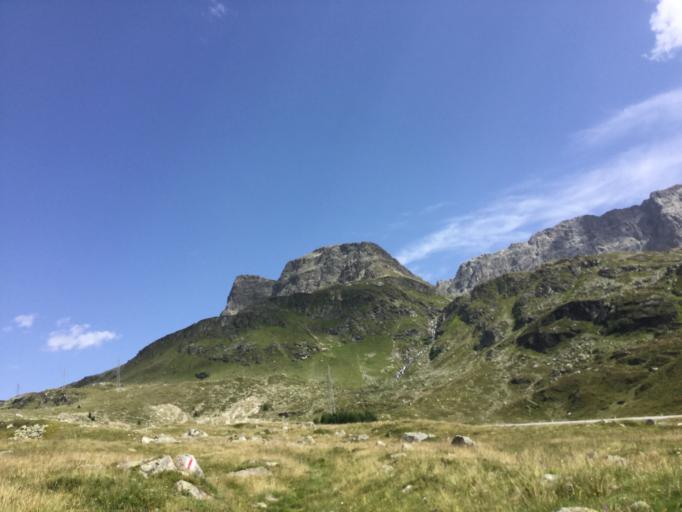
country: CH
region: Grisons
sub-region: Maloja District
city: Silvaplana
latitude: 46.4652
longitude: 9.7001
